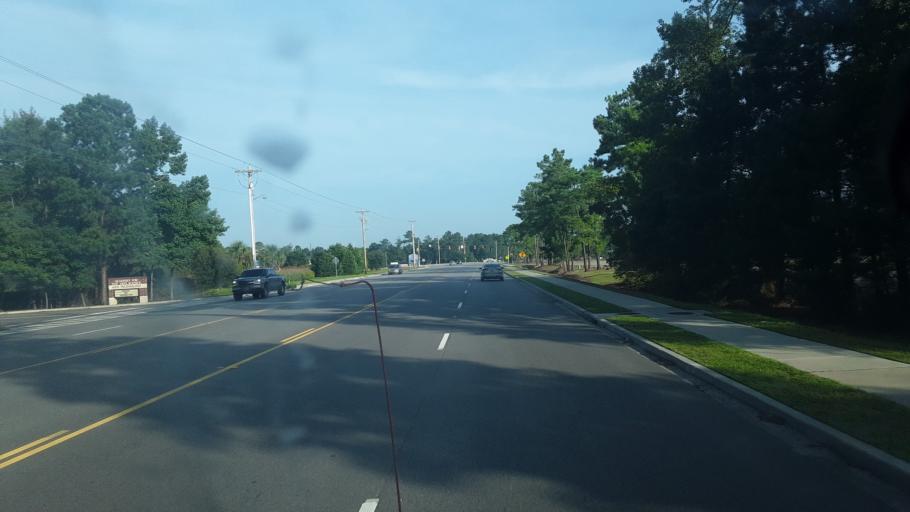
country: US
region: South Carolina
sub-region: Horry County
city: Myrtle Beach
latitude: 33.7649
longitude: -78.8637
